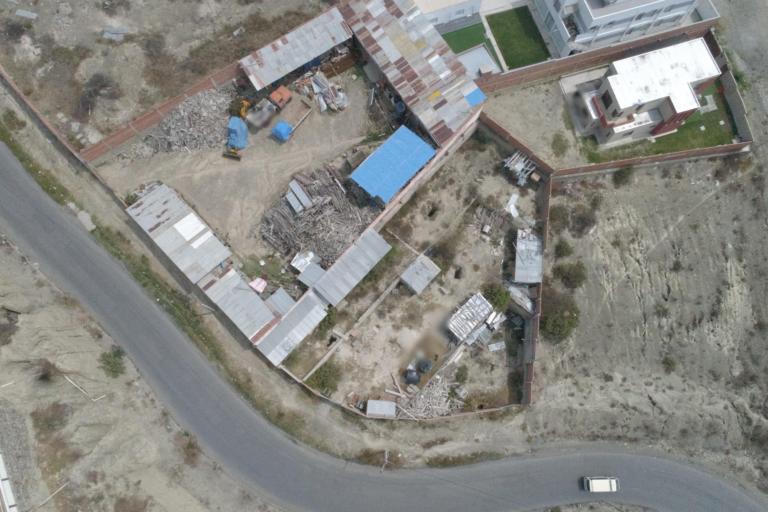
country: BO
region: La Paz
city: La Paz
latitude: -16.6020
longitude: -68.0696
